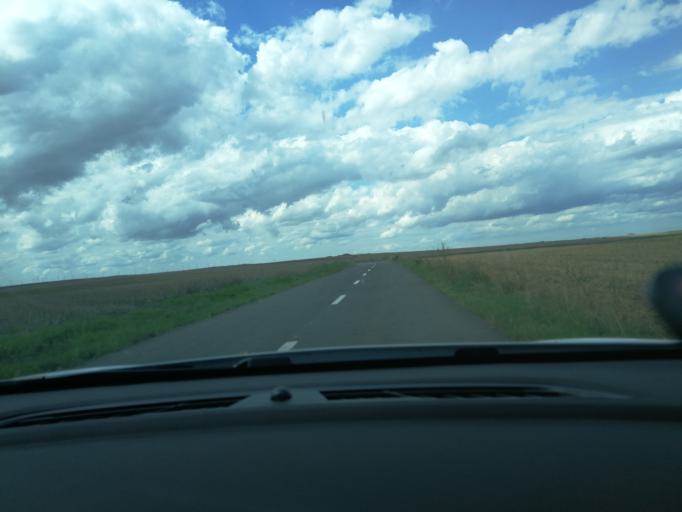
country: RO
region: Constanta
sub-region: Comuna Istria
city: Istria
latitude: 44.5389
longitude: 28.7239
